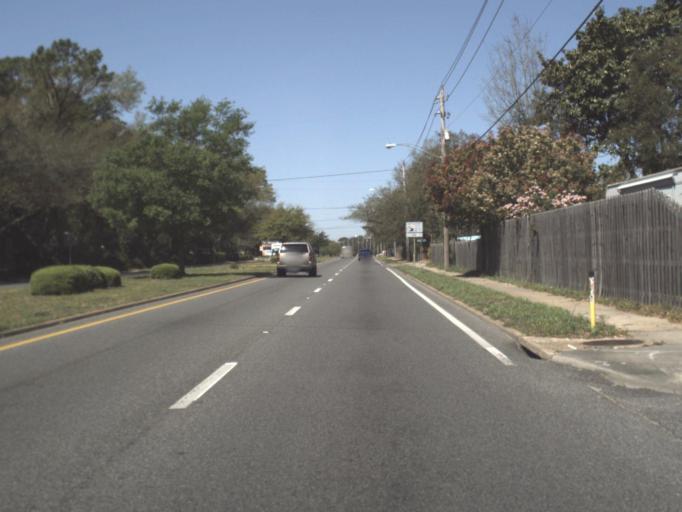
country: US
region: Florida
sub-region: Okaloosa County
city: Mary Esther
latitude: 30.4083
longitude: -86.6437
